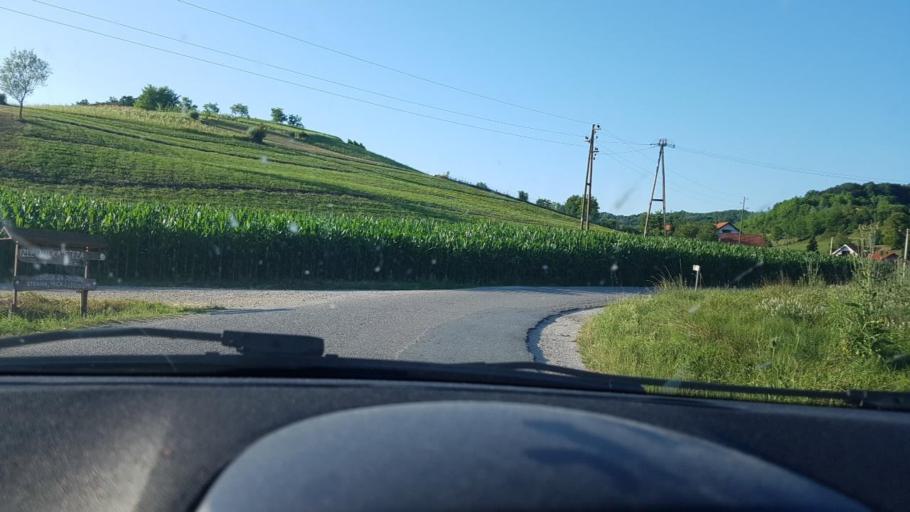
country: HR
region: Krapinsko-Zagorska
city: Zabok
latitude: 46.0855
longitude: 15.9354
